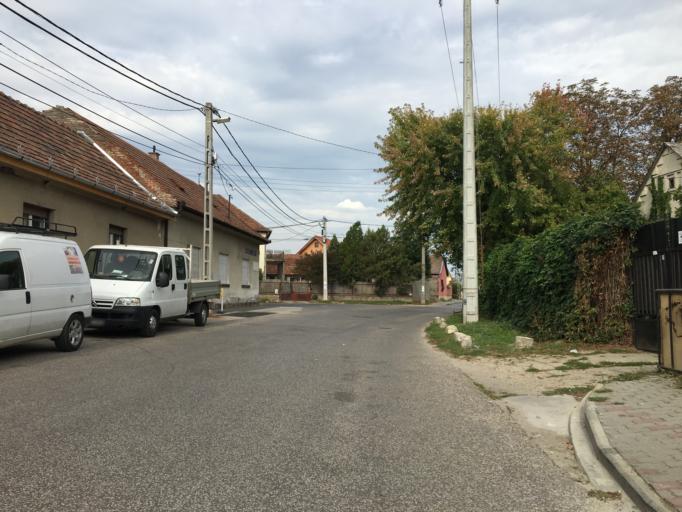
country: HU
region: Pest
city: Szigetszentmiklos
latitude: 47.3484
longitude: 19.0503
